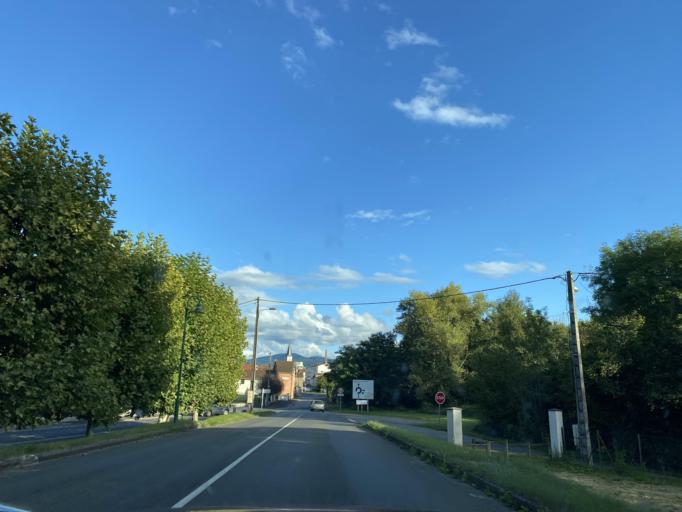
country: FR
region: Auvergne
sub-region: Departement du Puy-de-Dome
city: Puy-Guillaume
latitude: 45.9619
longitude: 3.4662
